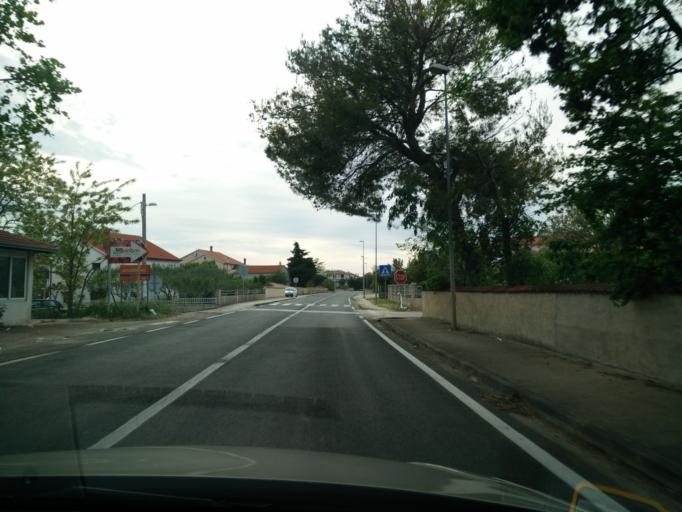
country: HR
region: Zadarska
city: Turanj
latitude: 43.9672
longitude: 15.4120
